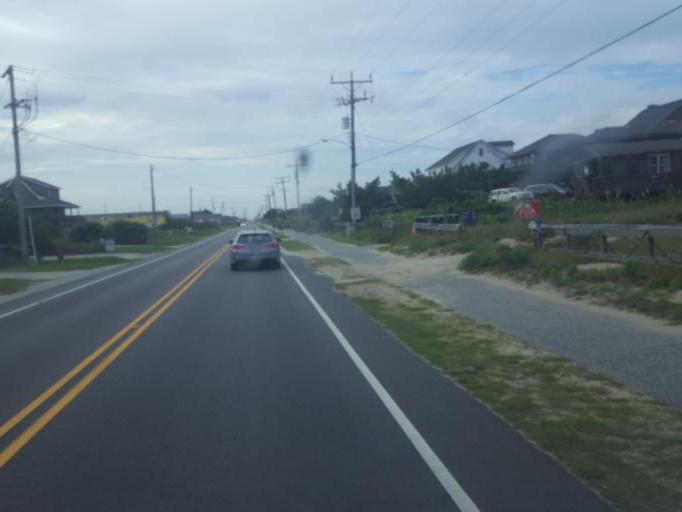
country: US
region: North Carolina
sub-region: Dare County
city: Nags Head
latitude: 35.9514
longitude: -75.6208
